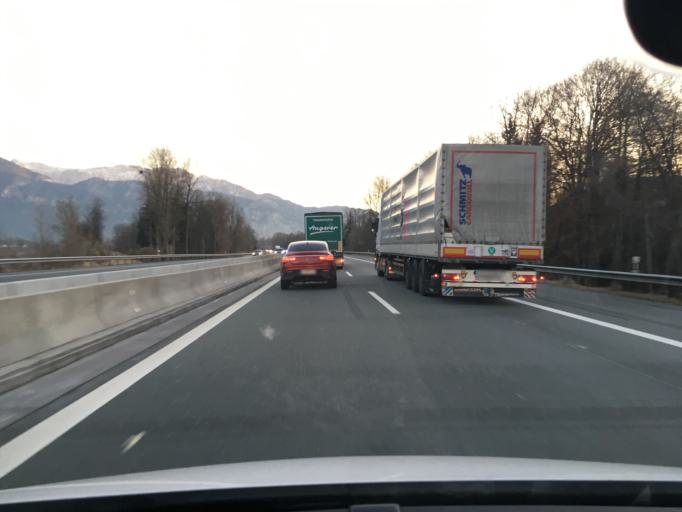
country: DE
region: Bavaria
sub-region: Upper Bavaria
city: Oberaudorf
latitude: 47.6605
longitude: 12.1834
